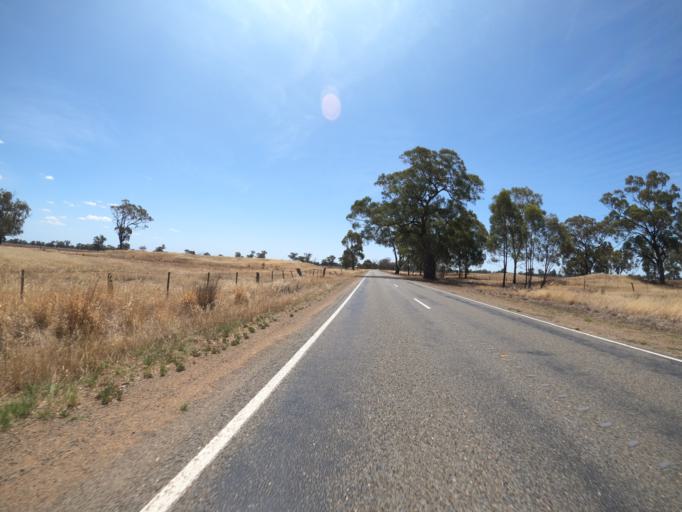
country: AU
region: Victoria
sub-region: Moira
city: Yarrawonga
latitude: -36.1942
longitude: 145.9670
